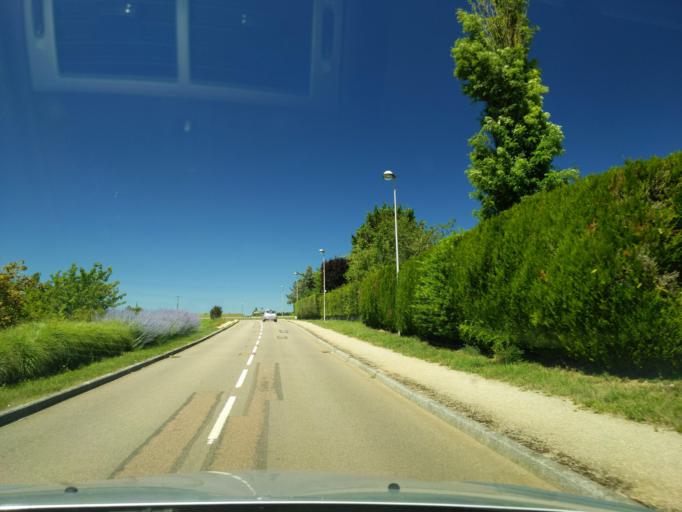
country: FR
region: Bourgogne
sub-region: Departement de la Cote-d'Or
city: Ruffey-les-Echirey
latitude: 47.3816
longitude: 5.0630
